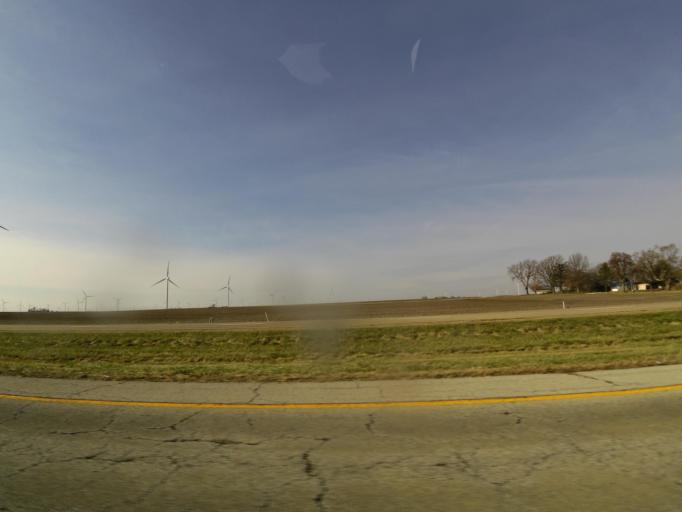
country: US
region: Illinois
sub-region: Macon County
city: Maroa
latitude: 40.0060
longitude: -88.9561
